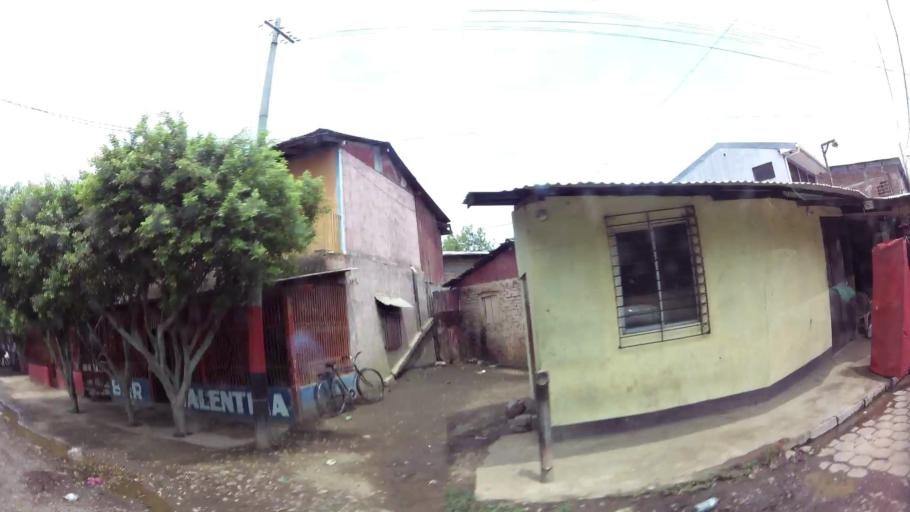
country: NI
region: Rivas
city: Rivas
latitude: 11.4396
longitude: -85.8338
